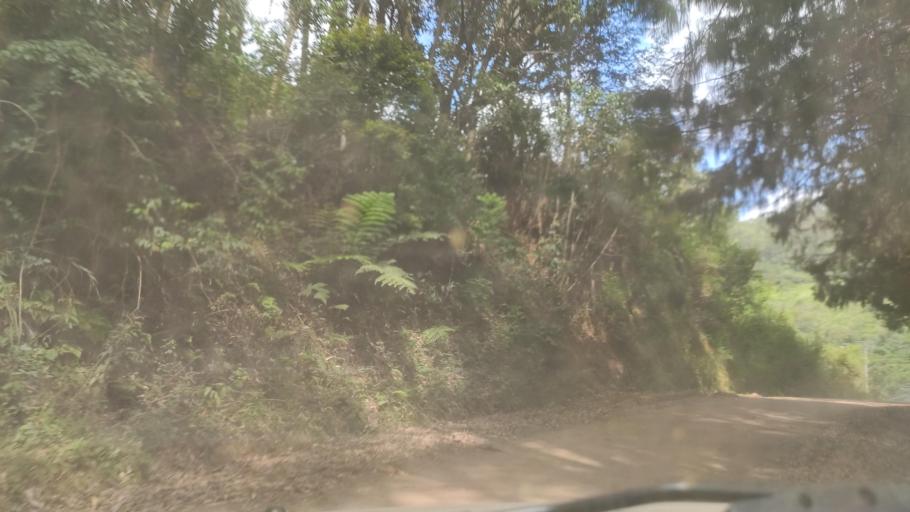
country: BR
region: Minas Gerais
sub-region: Camanducaia
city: Camanducaia
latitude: -22.7681
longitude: -45.9996
